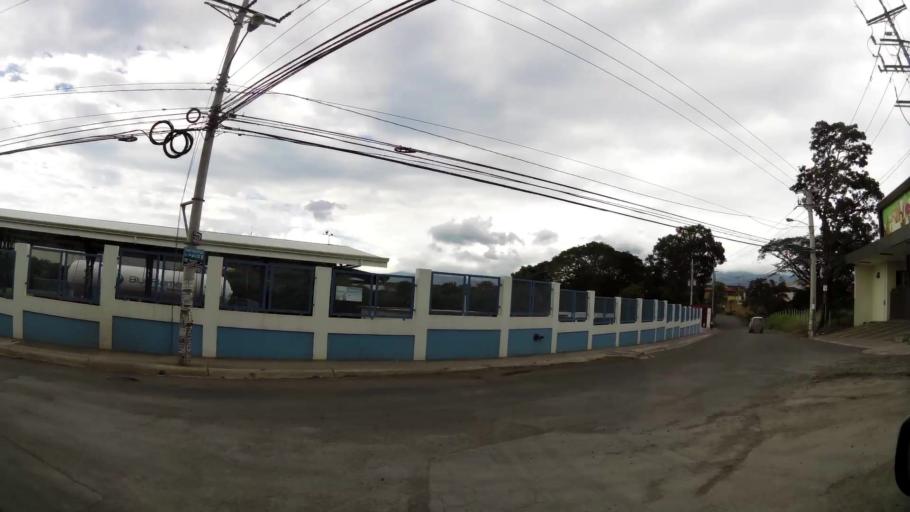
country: CR
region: Heredia
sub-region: Canton de Belen
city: San Antonio
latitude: 9.9620
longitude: -84.1957
